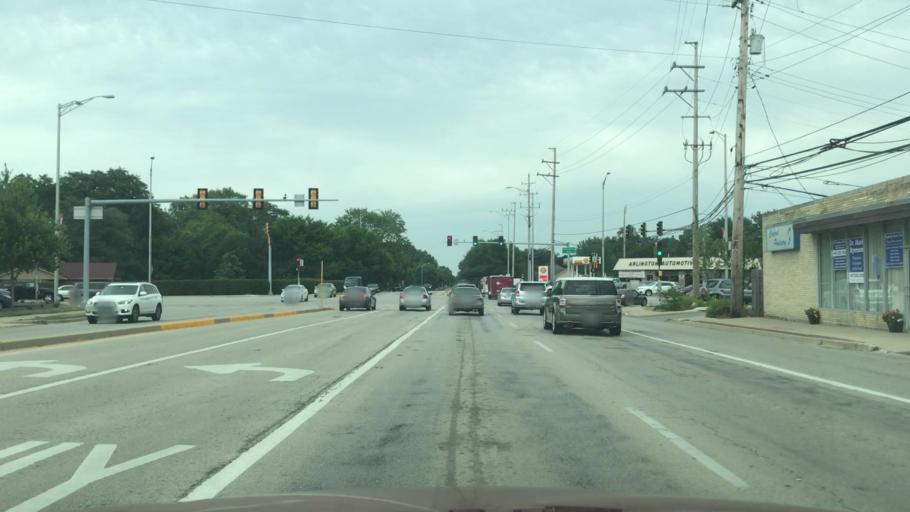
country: US
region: Illinois
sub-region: Cook County
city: Arlington Heights
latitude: 42.0665
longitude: -87.9809
